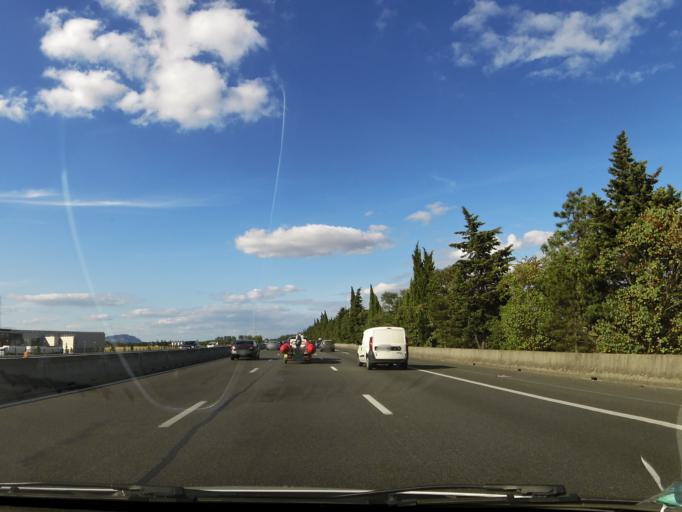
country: FR
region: Rhone-Alpes
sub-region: Departement de la Drome
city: Livron-sur-Drome
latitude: 44.8126
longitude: 4.8557
